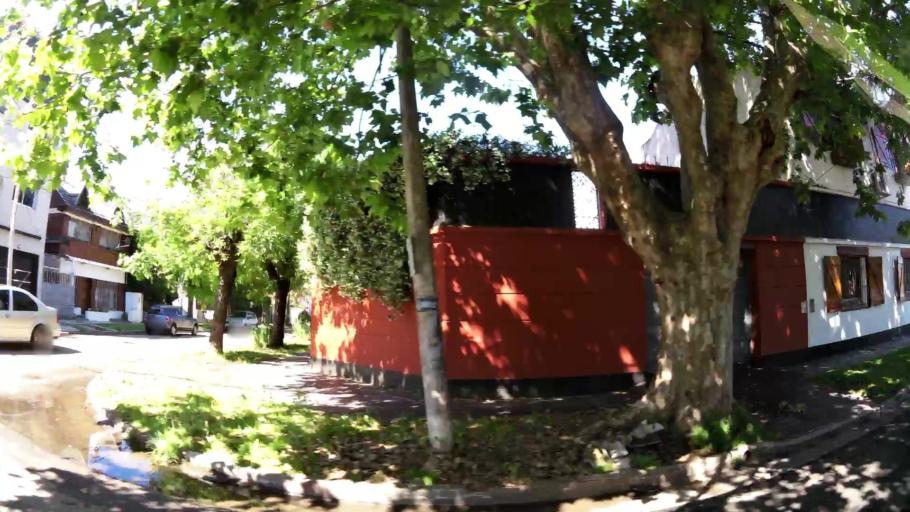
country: AR
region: Buenos Aires
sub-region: Partido de Quilmes
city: Quilmes
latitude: -34.7010
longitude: -58.2999
